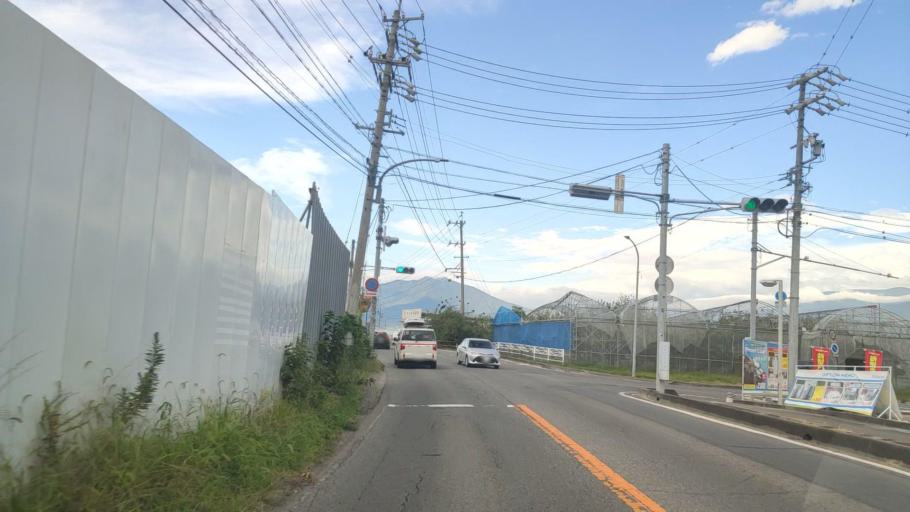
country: JP
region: Nagano
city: Nakano
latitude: 36.7237
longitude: 138.3338
